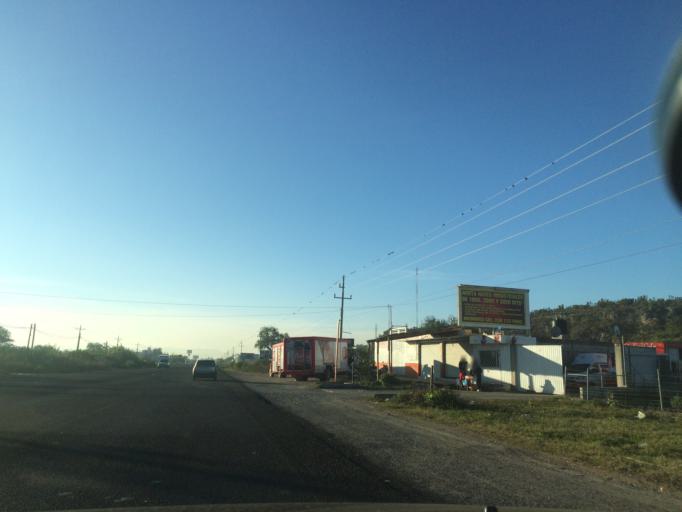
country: MX
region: Puebla
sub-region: Santiago Miahuatlan
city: San Jose Monte Chiquito
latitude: 18.4837
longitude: -97.4503
